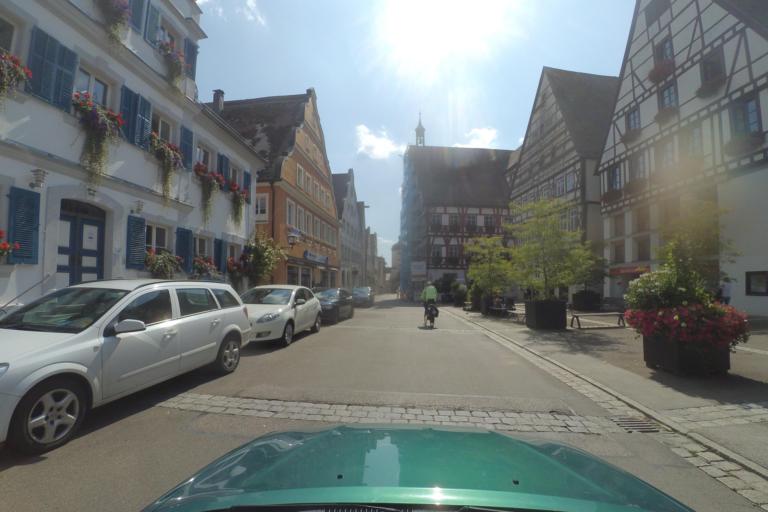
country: DE
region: Bavaria
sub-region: Swabia
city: Oettingen in Bayern
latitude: 48.9527
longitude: 10.6039
